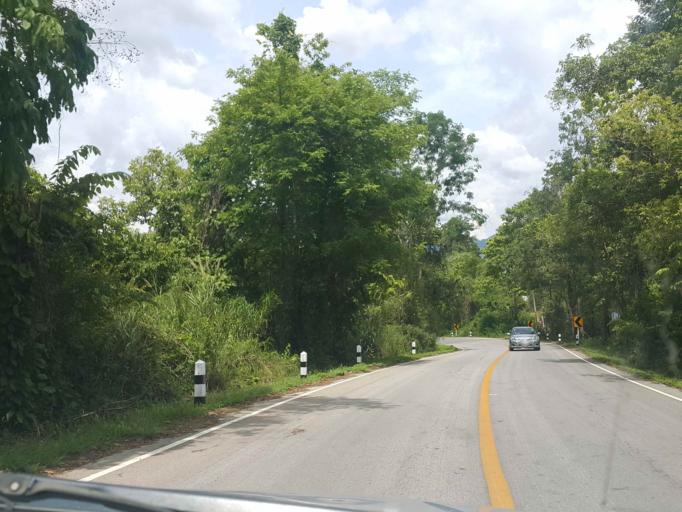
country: TH
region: Nan
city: Ban Luang
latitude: 18.8443
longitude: 100.4066
